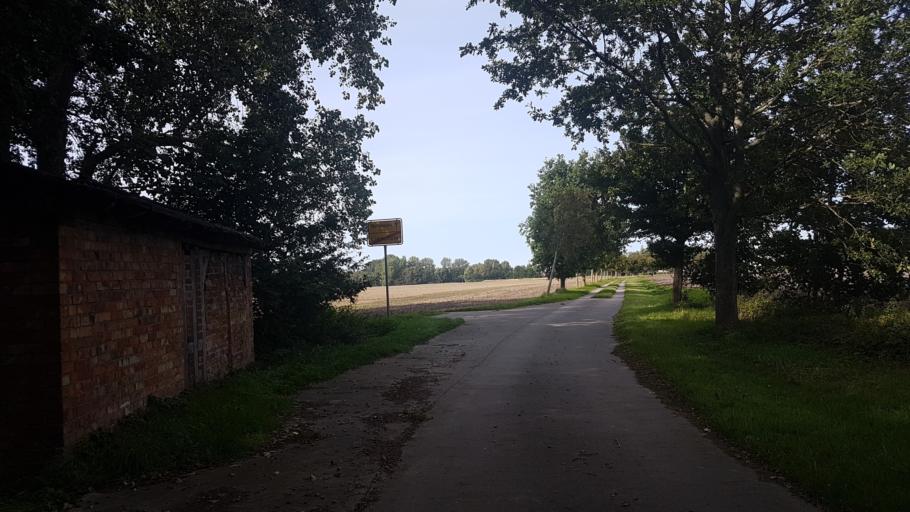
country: DE
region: Mecklenburg-Vorpommern
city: Gingst
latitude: 54.4426
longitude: 13.1842
